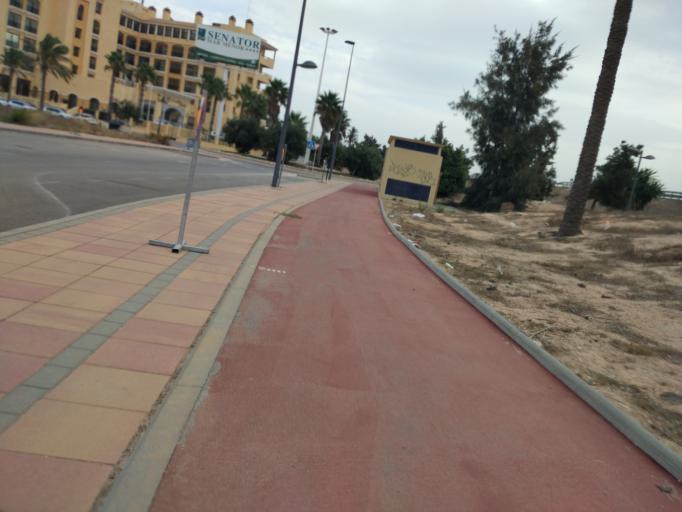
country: ES
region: Murcia
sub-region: Murcia
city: Los Alcazares
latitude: 37.7292
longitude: -0.8710
